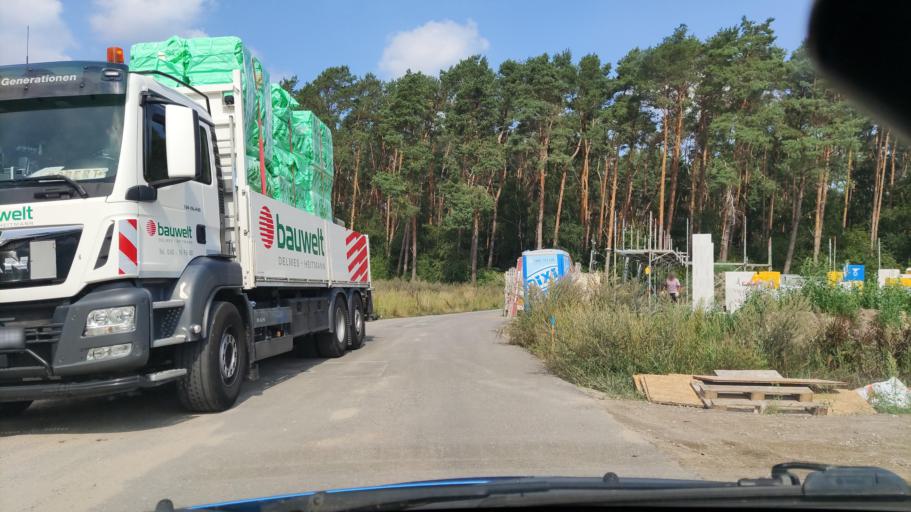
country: DE
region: Lower Saxony
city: Barum
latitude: 53.3440
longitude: 10.4126
